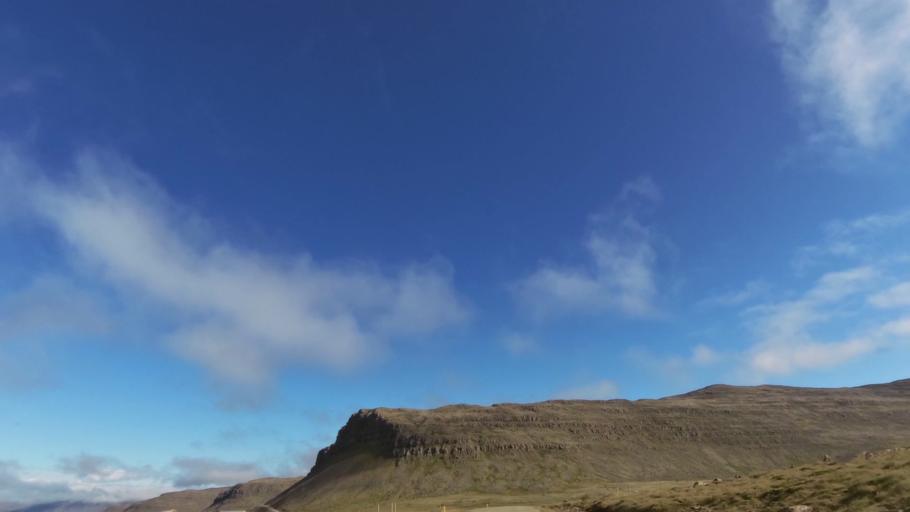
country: IS
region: West
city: Olafsvik
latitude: 65.5732
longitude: -24.0639
